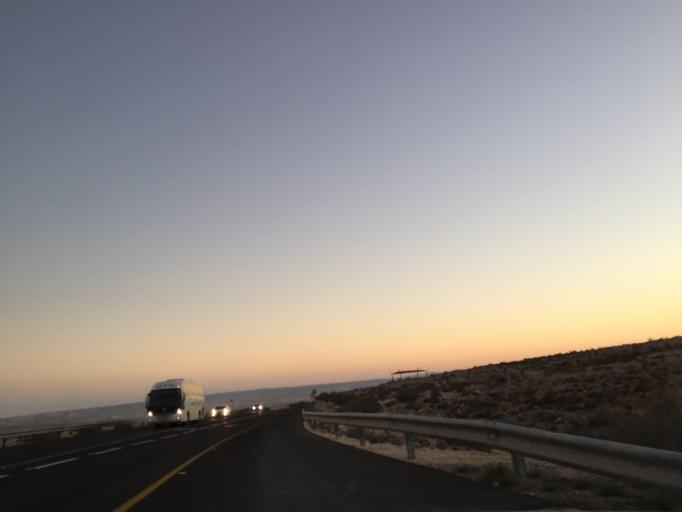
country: IL
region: Southern District
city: Midreshet Ben-Gurion
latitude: 30.8898
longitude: 34.7921
